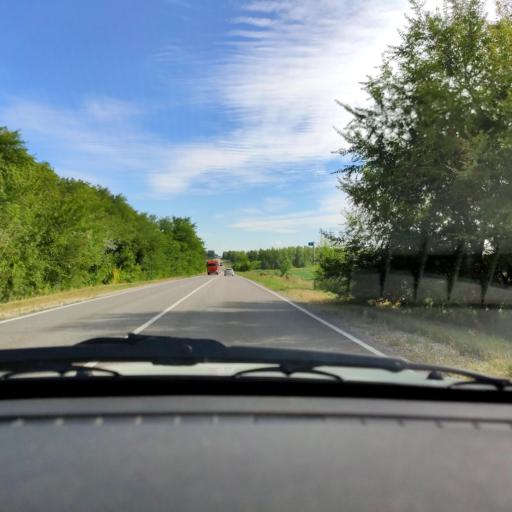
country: RU
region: Voronezj
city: Volya
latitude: 51.7156
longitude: 39.5364
